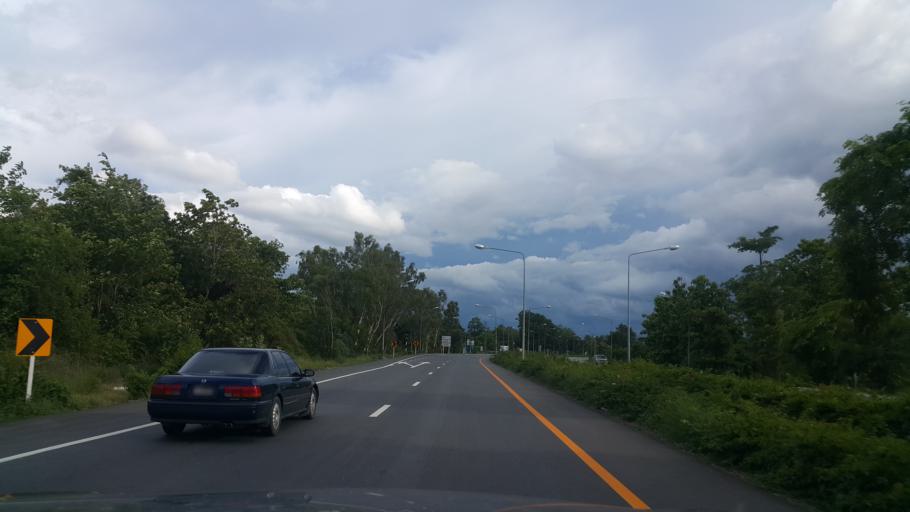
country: TH
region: Tak
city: Ban Tak
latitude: 16.9641
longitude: 99.1315
